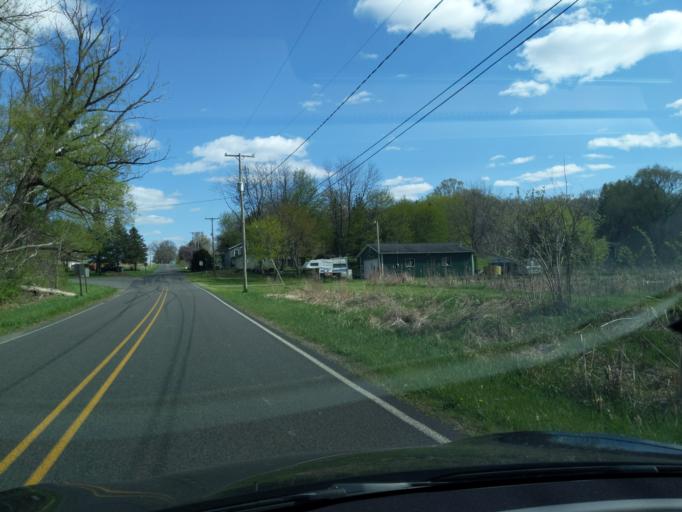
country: US
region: Michigan
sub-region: Ingham County
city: Leslie
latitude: 42.3721
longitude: -84.5390
